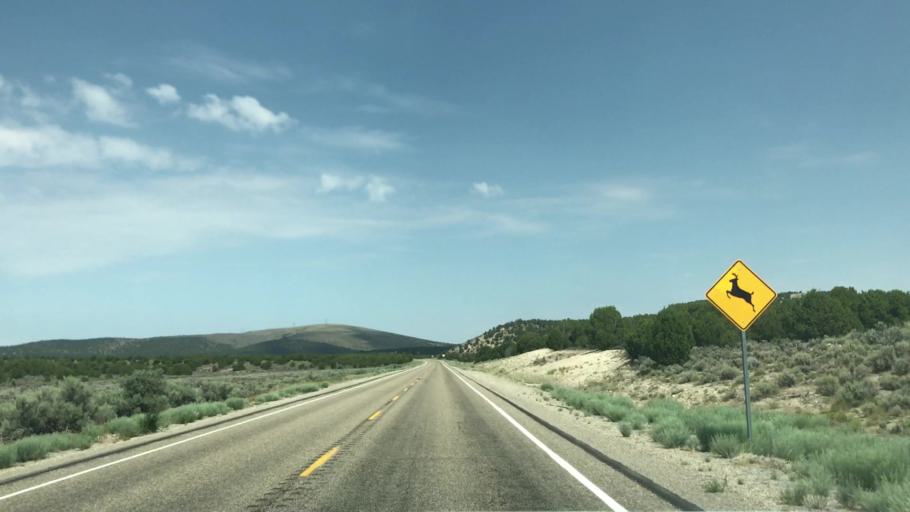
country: US
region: Nevada
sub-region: White Pine County
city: Ely
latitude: 39.3765
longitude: -115.0624
